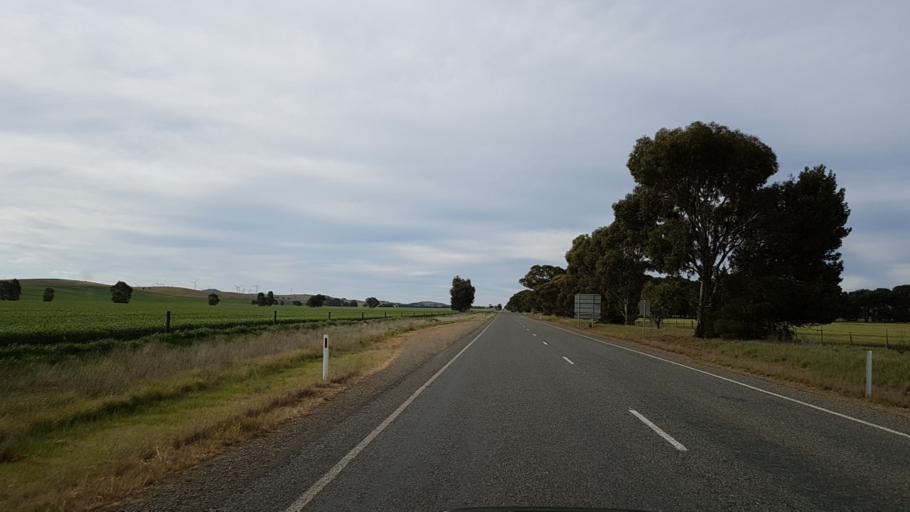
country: AU
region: South Australia
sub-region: Northern Areas
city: Jamestown
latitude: -33.1879
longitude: 138.6104
